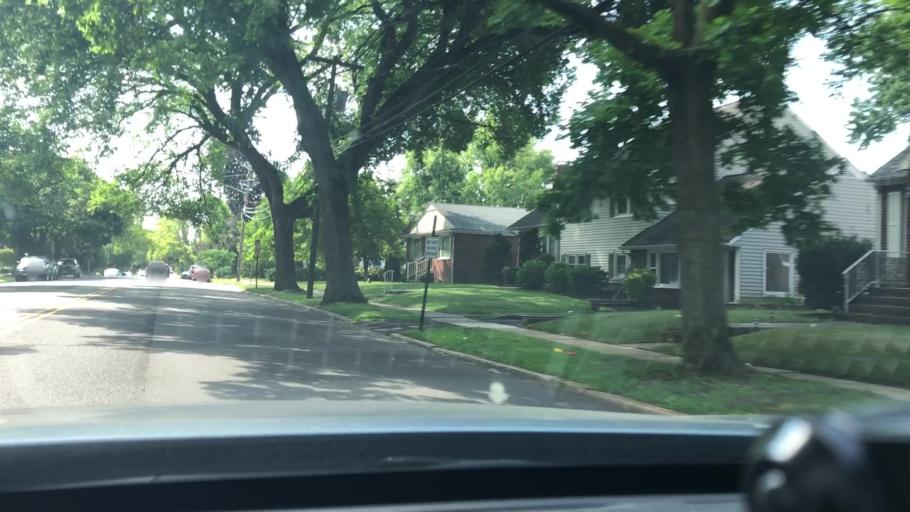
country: US
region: New Jersey
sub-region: Union County
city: Winfield
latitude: 40.6413
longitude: -74.2698
